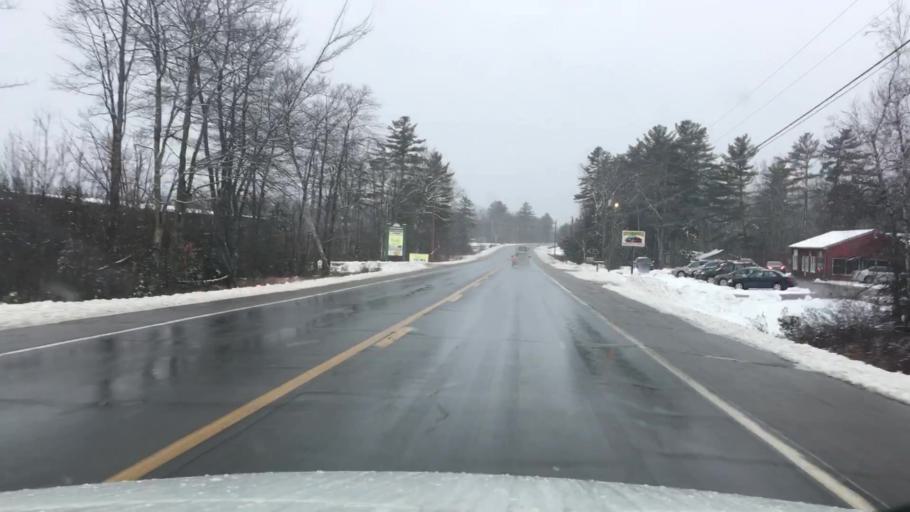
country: US
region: Maine
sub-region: Knox County
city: Warren
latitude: 44.1541
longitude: -69.1859
